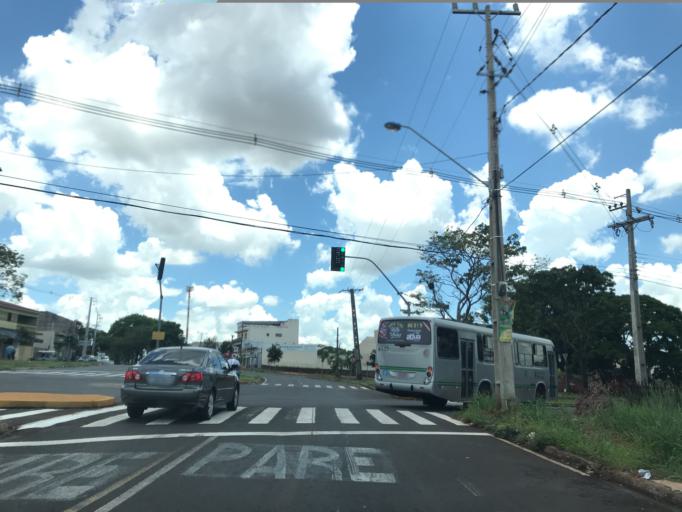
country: BR
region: Parana
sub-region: Maringa
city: Maringa
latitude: -23.3899
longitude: -51.9157
